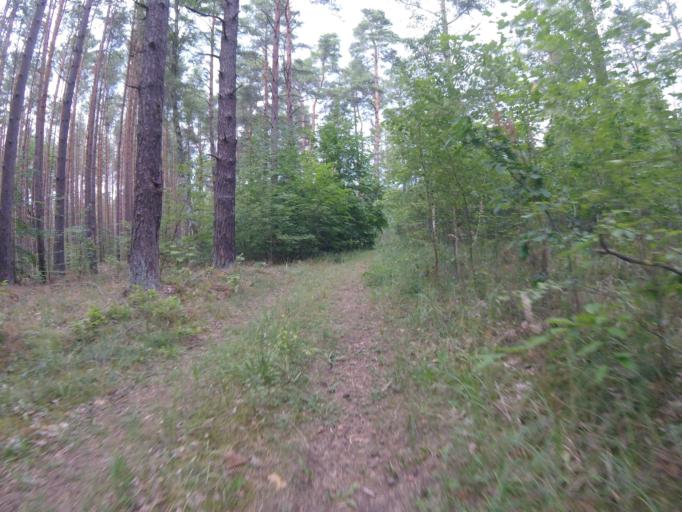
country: DE
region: Brandenburg
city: Wildau
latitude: 52.3324
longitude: 13.6686
